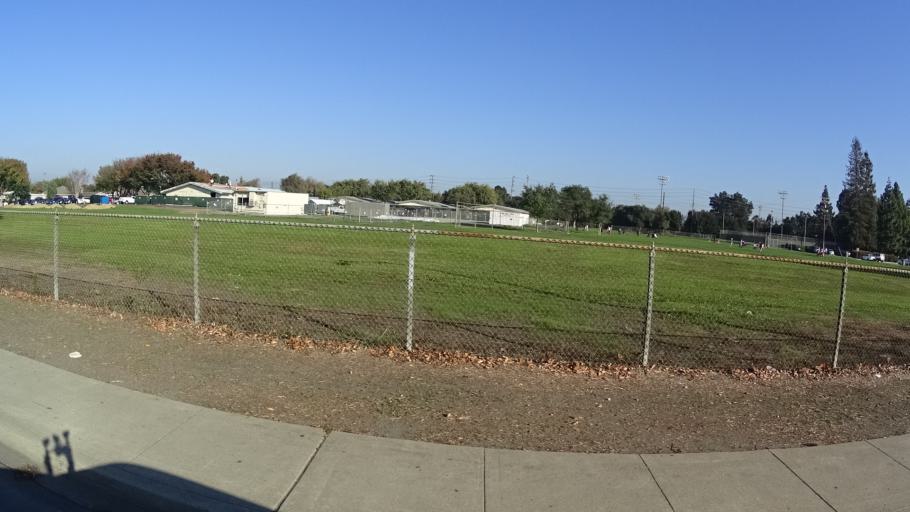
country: US
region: California
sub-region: Santa Clara County
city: Santa Clara
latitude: 37.3443
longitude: -121.9776
